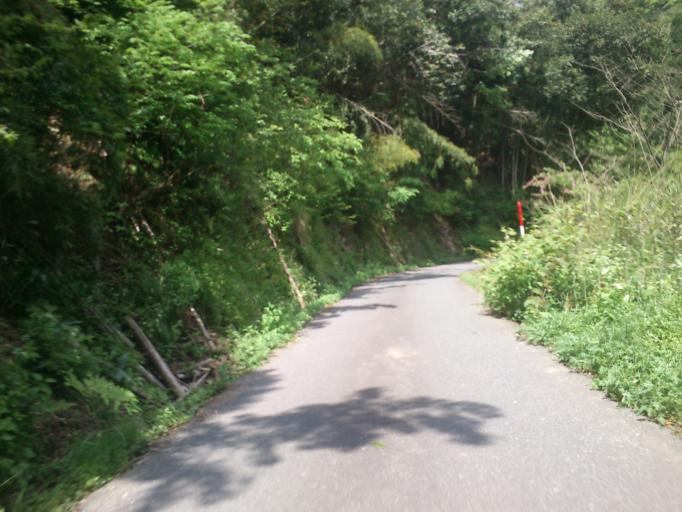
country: JP
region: Kyoto
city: Miyazu
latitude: 35.6673
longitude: 135.1601
